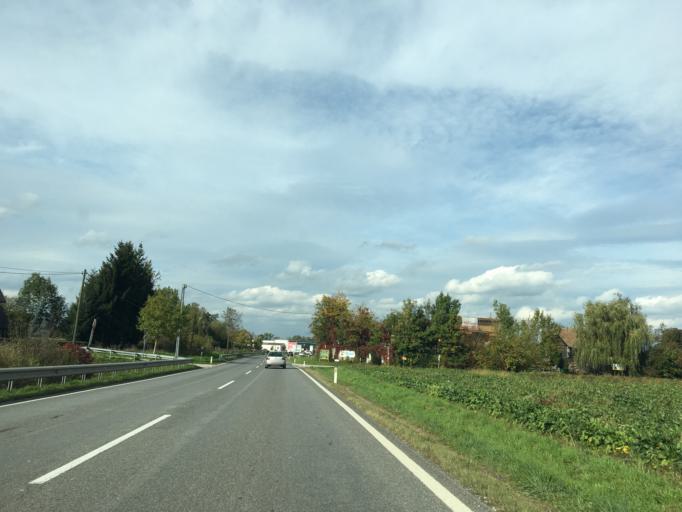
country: AT
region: Upper Austria
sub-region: Politischer Bezirk Urfahr-Umgebung
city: Feldkirchen an der Donau
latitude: 48.2931
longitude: 14.0101
